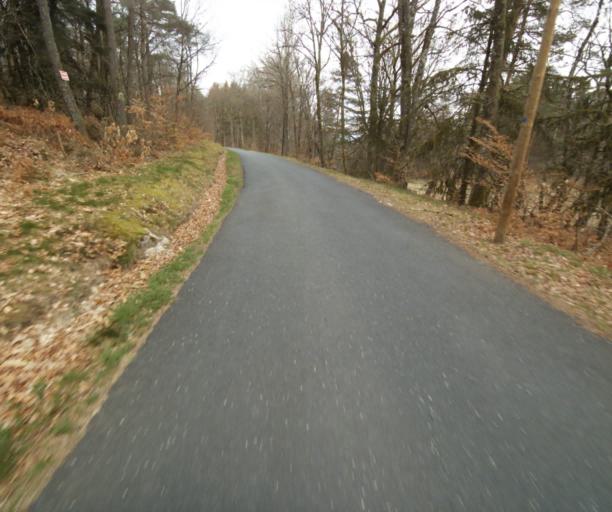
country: FR
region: Limousin
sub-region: Departement de la Correze
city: Correze
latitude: 45.3006
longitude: 1.9143
